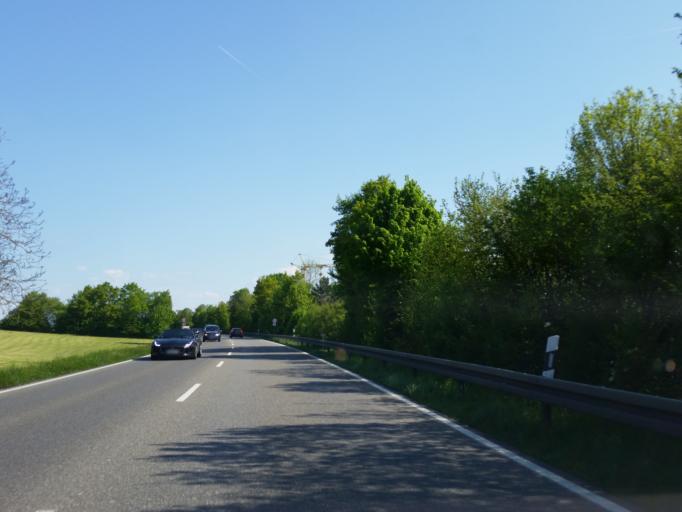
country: DE
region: Baden-Wuerttemberg
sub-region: Freiburg Region
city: Allensbach
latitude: 47.7163
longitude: 9.0760
